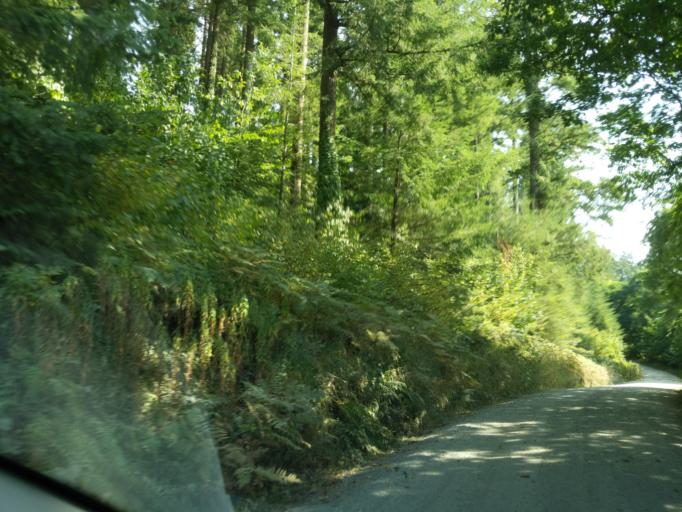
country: GB
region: England
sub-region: Devon
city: Winkleigh
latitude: 50.8820
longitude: -3.8582
